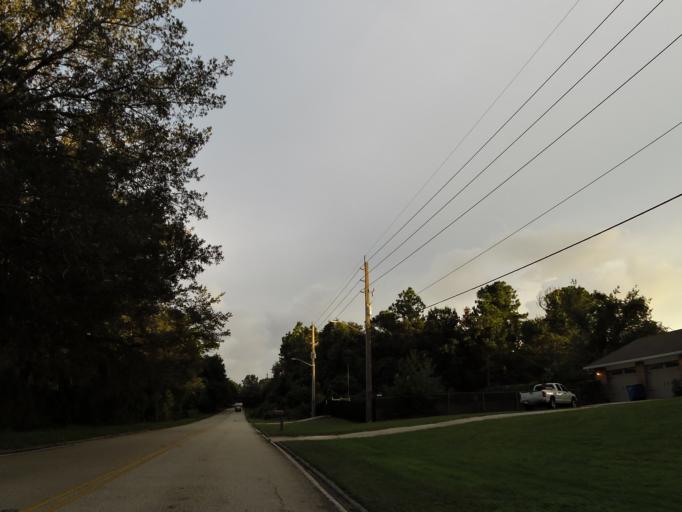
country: US
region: Florida
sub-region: Duval County
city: Atlantic Beach
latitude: 30.3767
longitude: -81.4890
